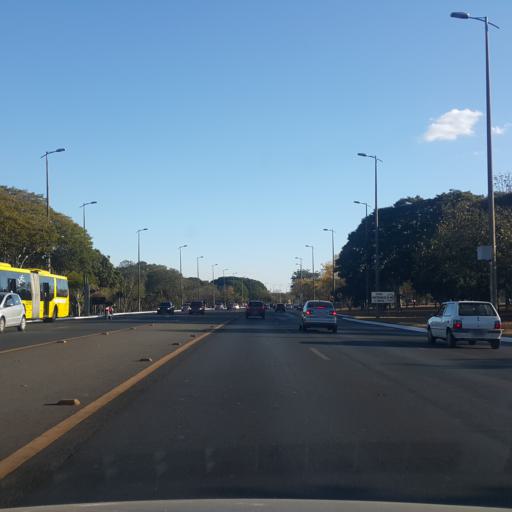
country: BR
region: Federal District
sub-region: Brasilia
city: Brasilia
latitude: -15.8013
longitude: -47.8859
